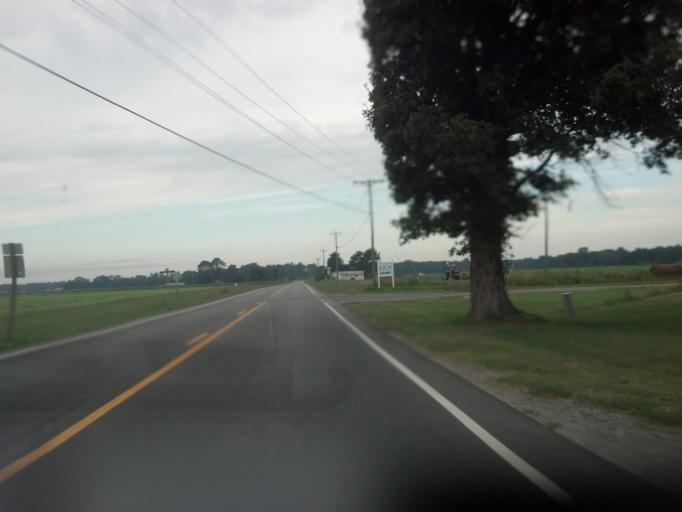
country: US
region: North Carolina
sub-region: Greene County
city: Maury
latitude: 35.4619
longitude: -77.5087
